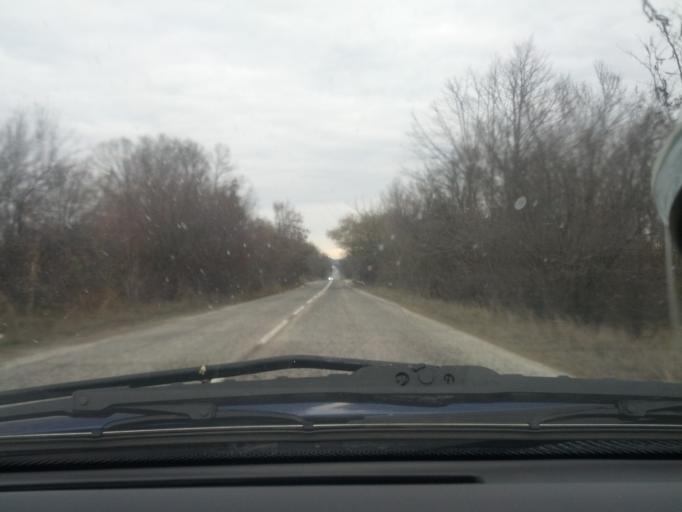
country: BG
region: Vratsa
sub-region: Obshtina Vratsa
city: Vratsa
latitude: 43.2967
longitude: 23.6590
